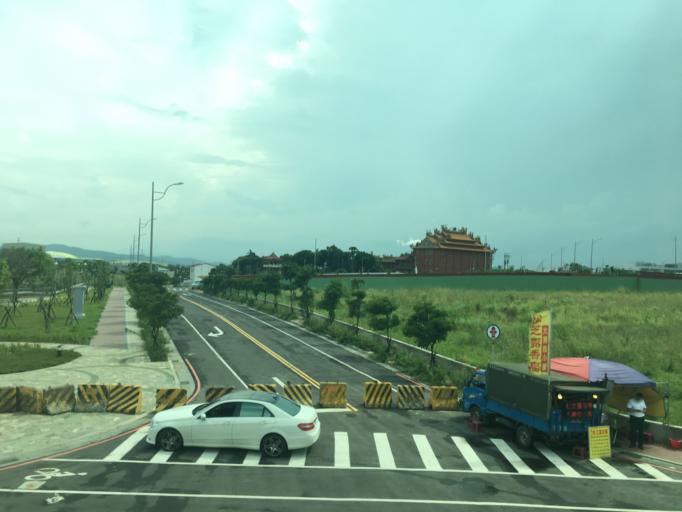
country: TW
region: Taiwan
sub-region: Taoyuan
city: Taoyuan
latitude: 25.0496
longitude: 121.3830
